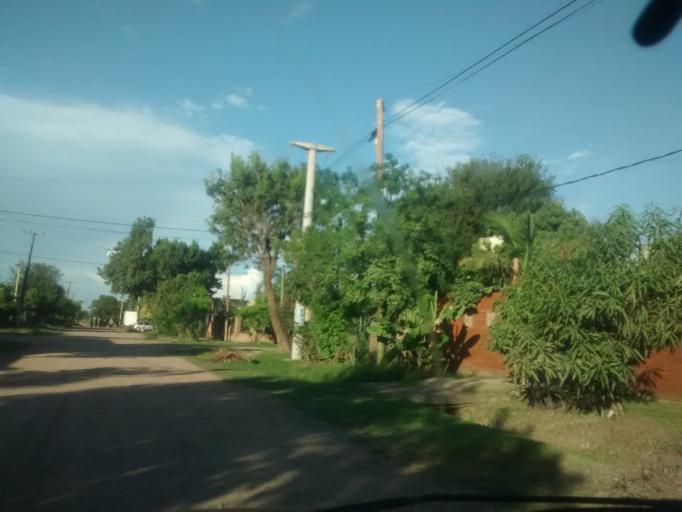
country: AR
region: Chaco
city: Resistencia
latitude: -27.4316
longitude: -58.9932
